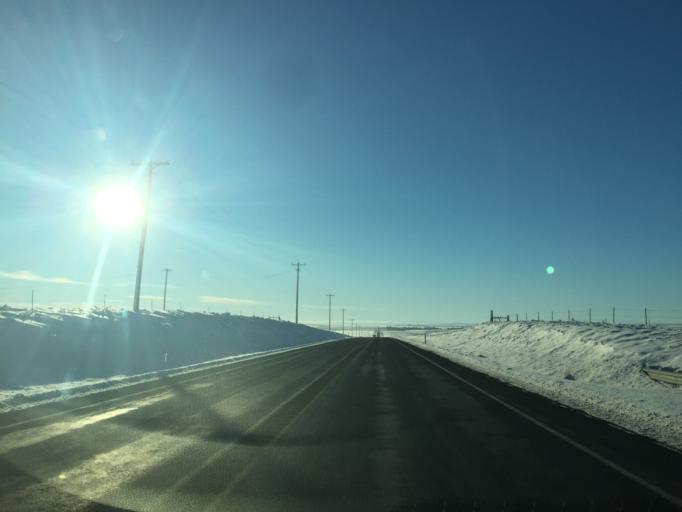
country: US
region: Washington
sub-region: Okanogan County
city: Coulee Dam
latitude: 47.7329
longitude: -118.8616
